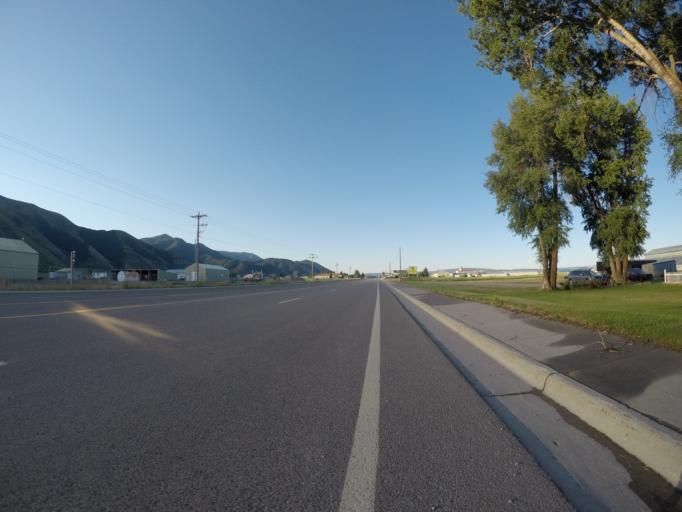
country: US
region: Wyoming
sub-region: Lincoln County
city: Afton
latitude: 42.7507
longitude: -110.9334
